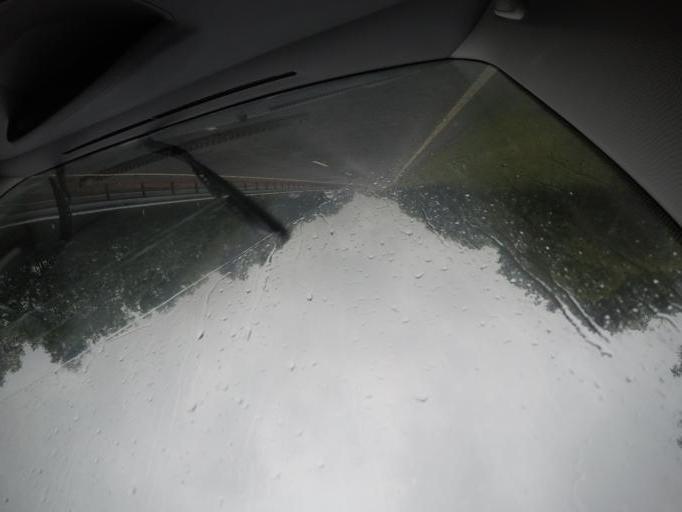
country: GB
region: Scotland
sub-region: Angus
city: Forfar
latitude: 56.5840
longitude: -2.9130
